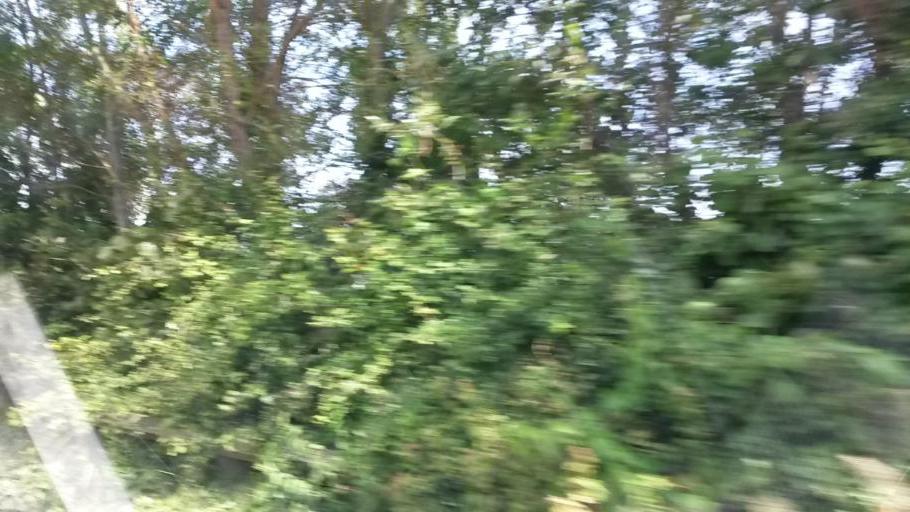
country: IE
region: Leinster
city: Lusk
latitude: 53.5061
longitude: -6.1809
